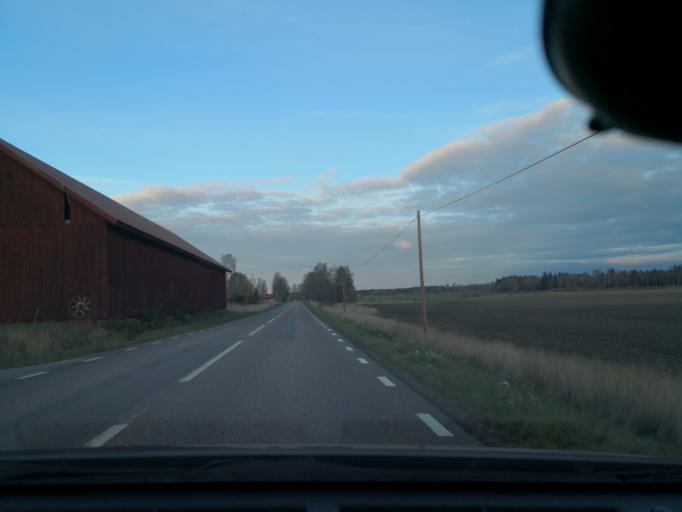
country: SE
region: Vaestmanland
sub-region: Vasteras
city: Tillberga
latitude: 59.6376
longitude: 16.6725
